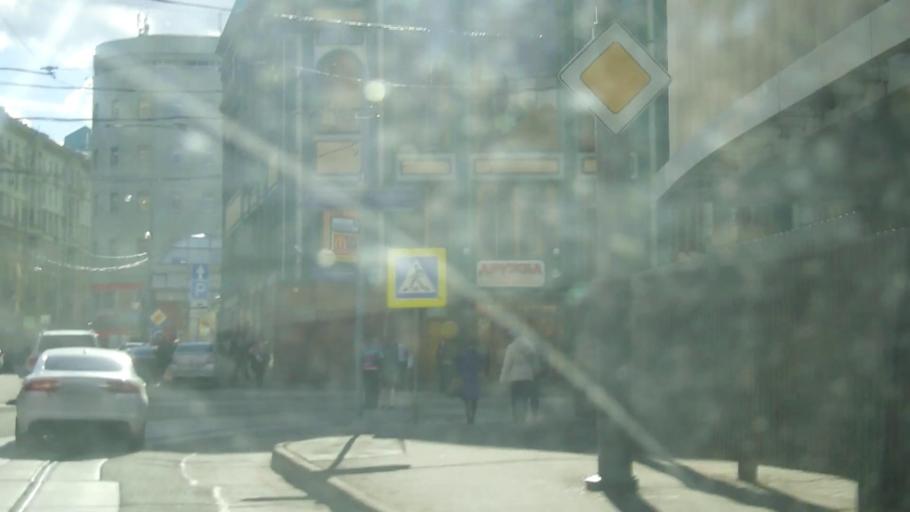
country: RU
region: Moscow
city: Mar'ina Roshcha
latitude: 55.7797
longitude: 37.6032
